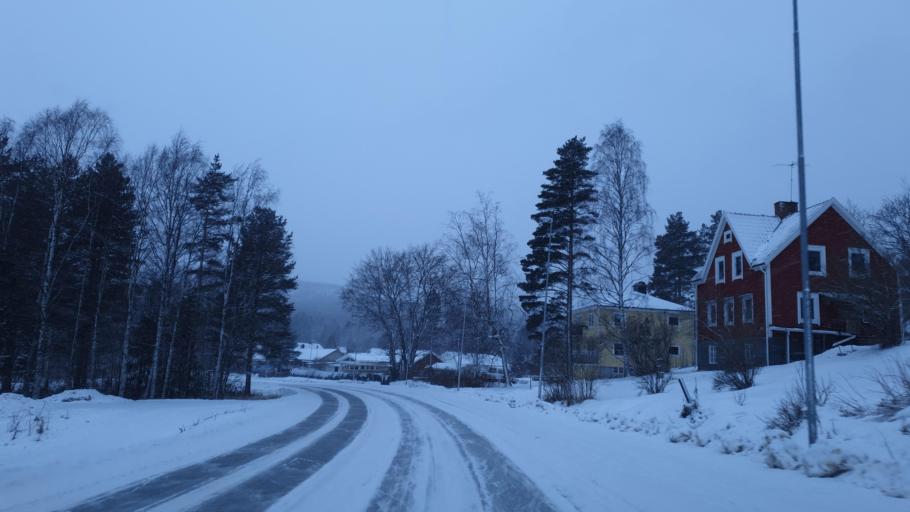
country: SE
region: Vaesternorrland
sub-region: OErnskoeldsviks Kommun
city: Ornskoldsvik
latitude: 63.2994
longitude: 18.6438
